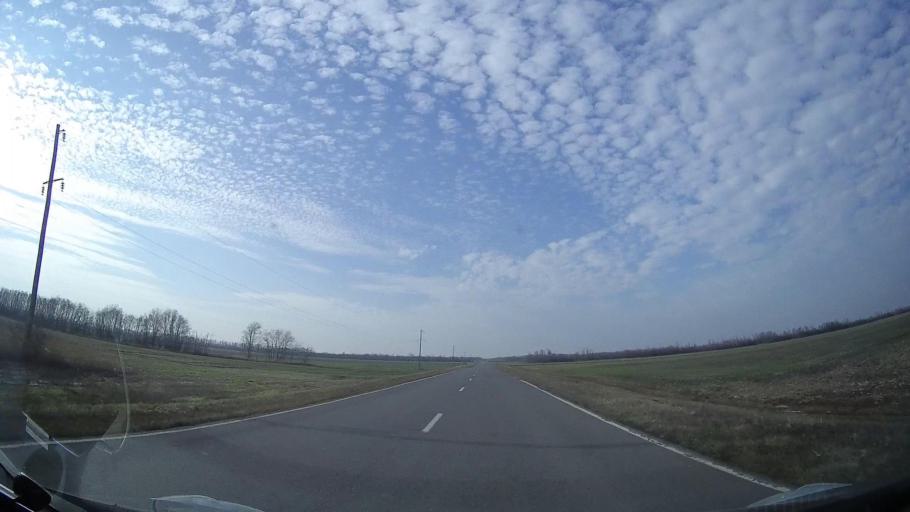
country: RU
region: Rostov
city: Veselyy
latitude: 46.9691
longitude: 40.6962
